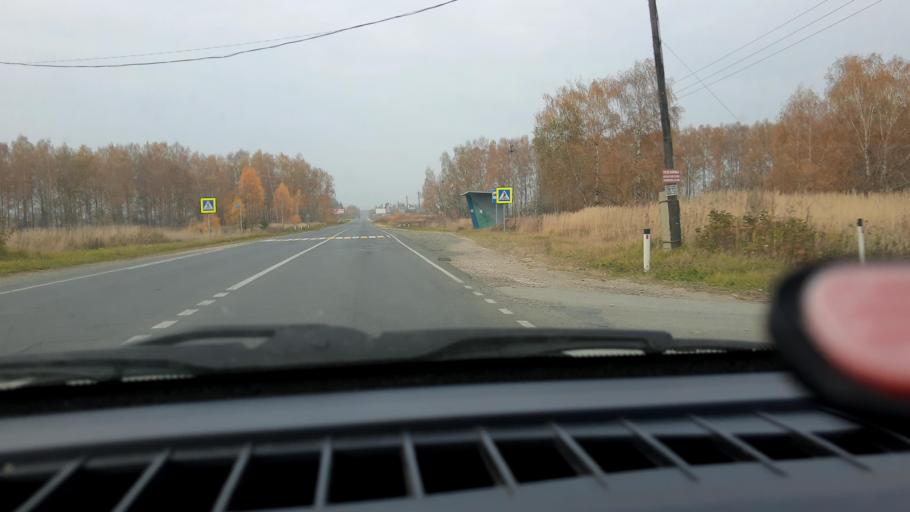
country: RU
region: Nizjnij Novgorod
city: Gorodets
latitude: 56.6298
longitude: 43.5398
